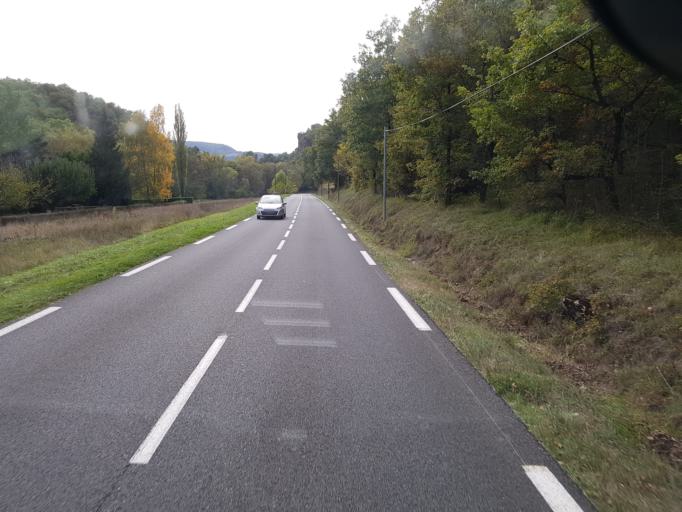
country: FR
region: Midi-Pyrenees
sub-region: Departement de l'Aveyron
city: Saint-Affrique
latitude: 43.9721
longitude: 2.9028
